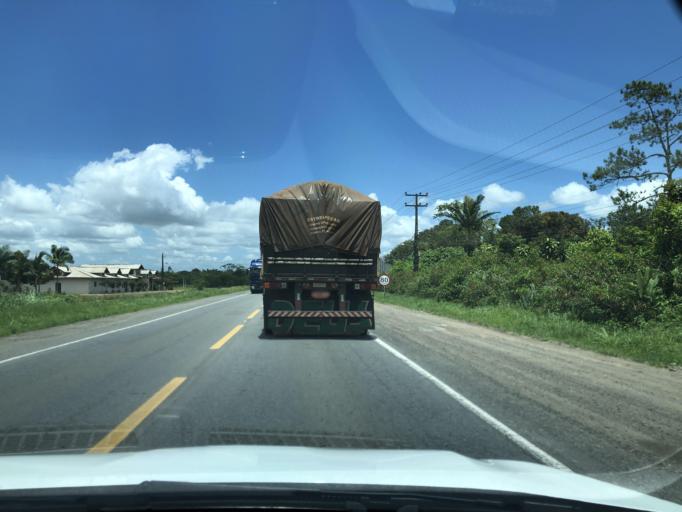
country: BR
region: Santa Catarina
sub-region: Sao Francisco Do Sul
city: Sao Francisco do Sul
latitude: -26.3705
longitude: -48.6941
